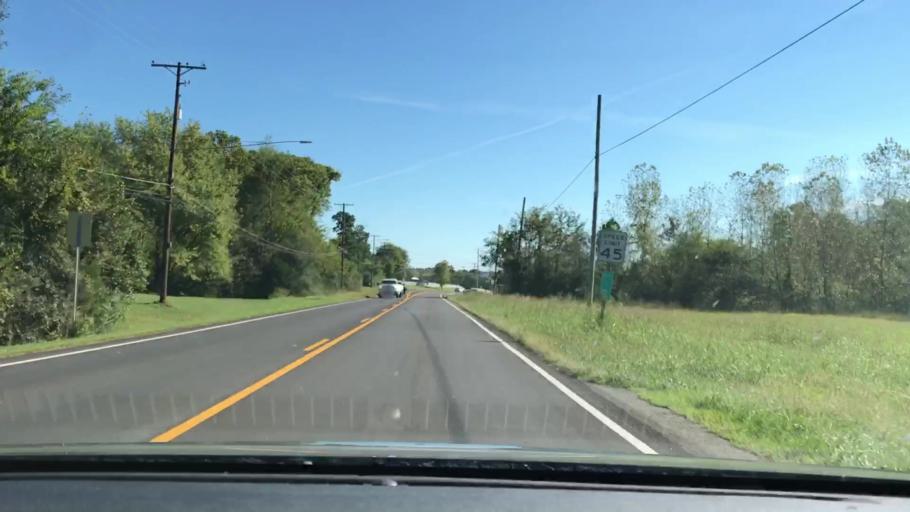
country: US
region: Kentucky
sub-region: Christian County
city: Hopkinsville
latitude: 36.8638
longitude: -87.4610
